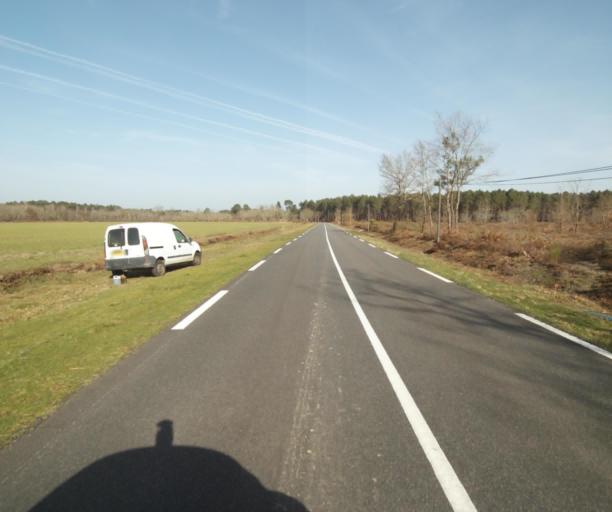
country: FR
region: Aquitaine
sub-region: Departement de la Gironde
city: Grignols
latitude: 44.2099
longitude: -0.1619
